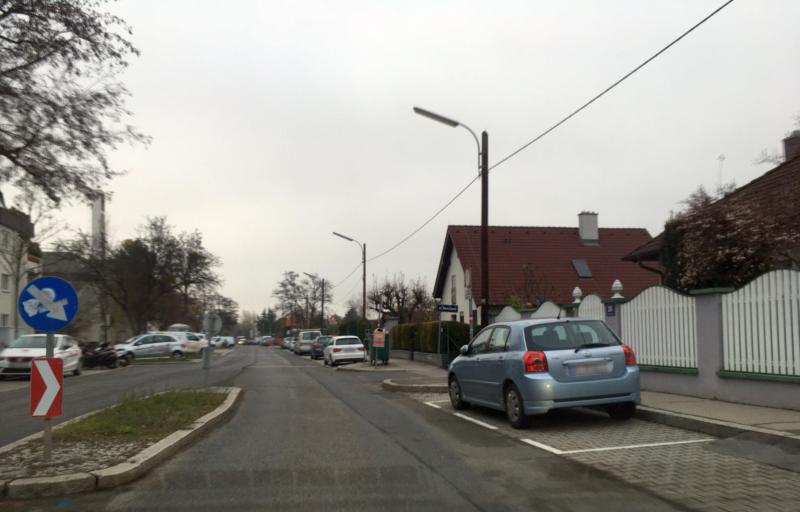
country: AT
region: Lower Austria
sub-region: Politischer Bezirk Wien-Umgebung
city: Gerasdorf bei Wien
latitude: 48.2166
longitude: 16.4571
